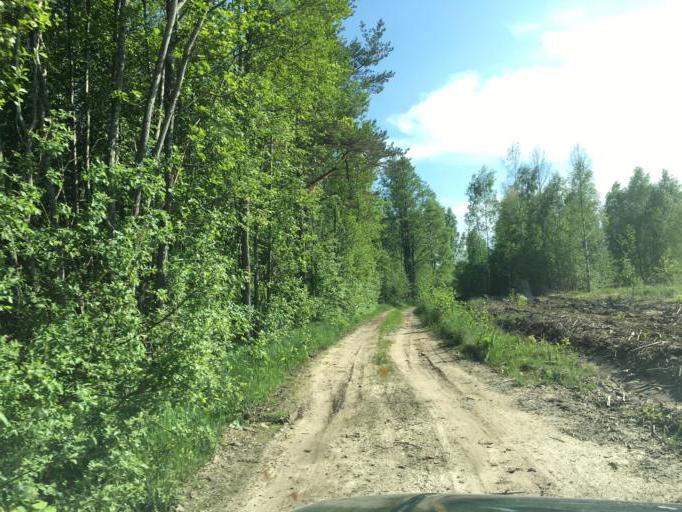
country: LV
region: Dundaga
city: Dundaga
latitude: 57.6021
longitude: 22.5078
